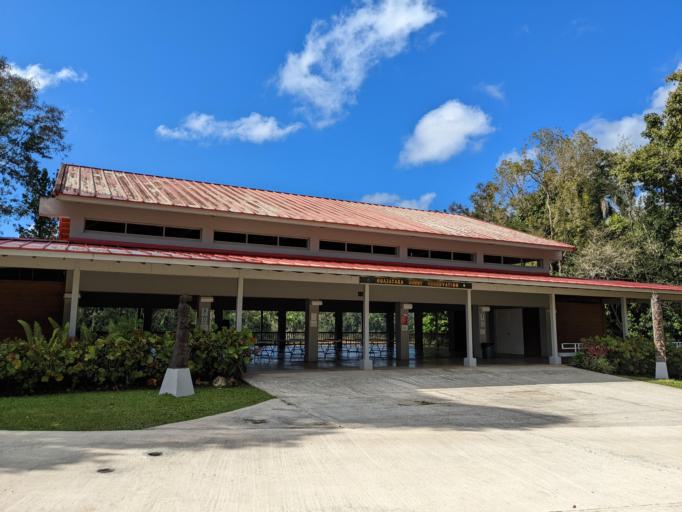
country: PR
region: San Sebastian
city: Juncal
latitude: 18.3687
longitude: -66.9199
